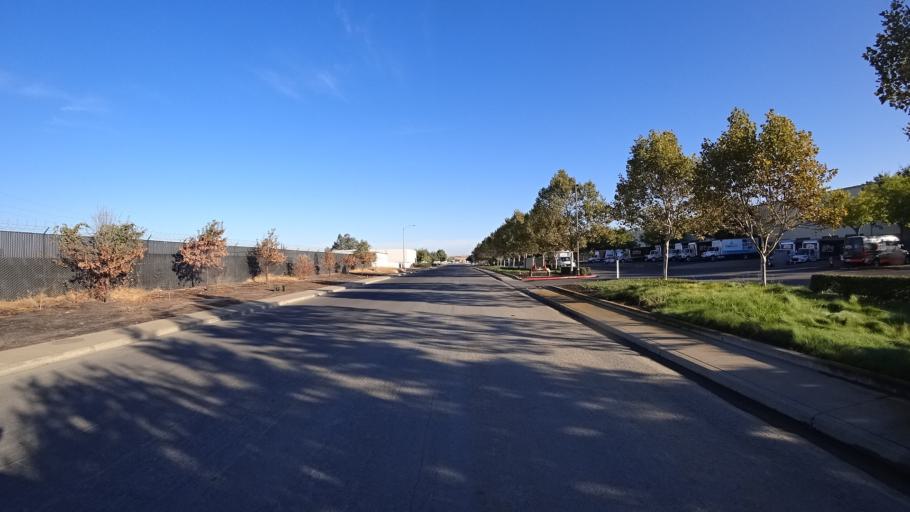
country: US
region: California
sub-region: Sacramento County
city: Florin
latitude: 38.5191
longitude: -121.3849
